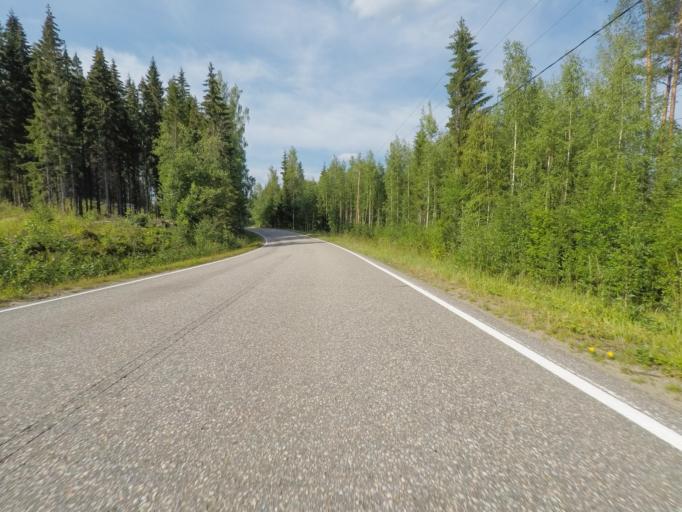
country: FI
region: Southern Savonia
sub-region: Savonlinna
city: Sulkava
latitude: 61.7770
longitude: 28.2394
